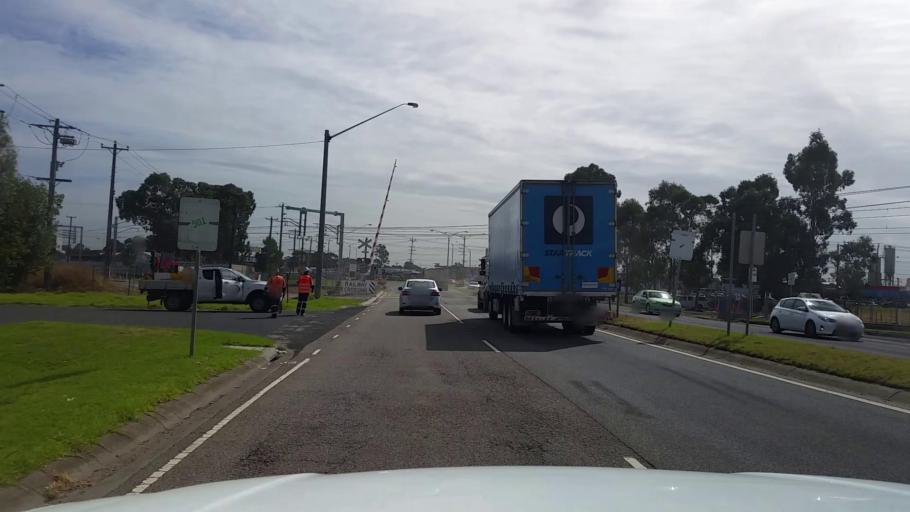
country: AU
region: Victoria
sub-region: Casey
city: Doveton
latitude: -38.0025
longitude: 145.2261
